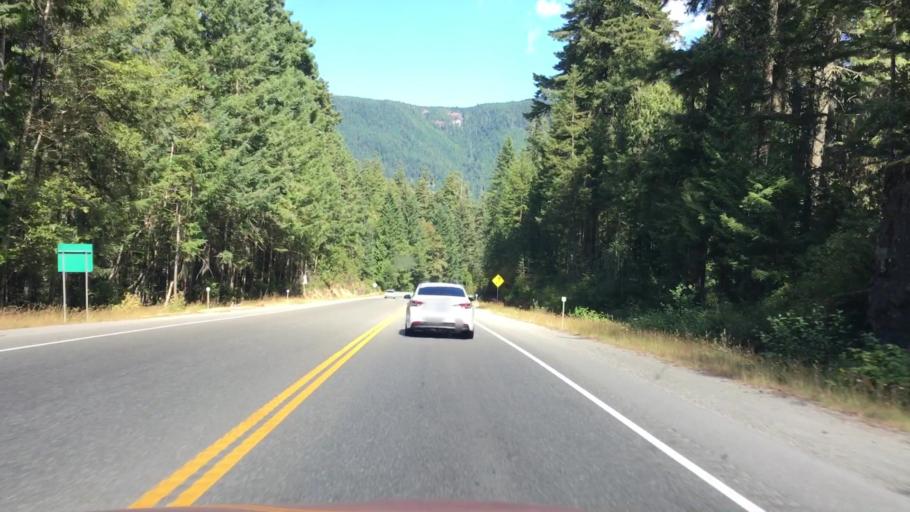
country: CA
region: British Columbia
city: Port Alberni
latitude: 49.2465
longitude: -124.6820
